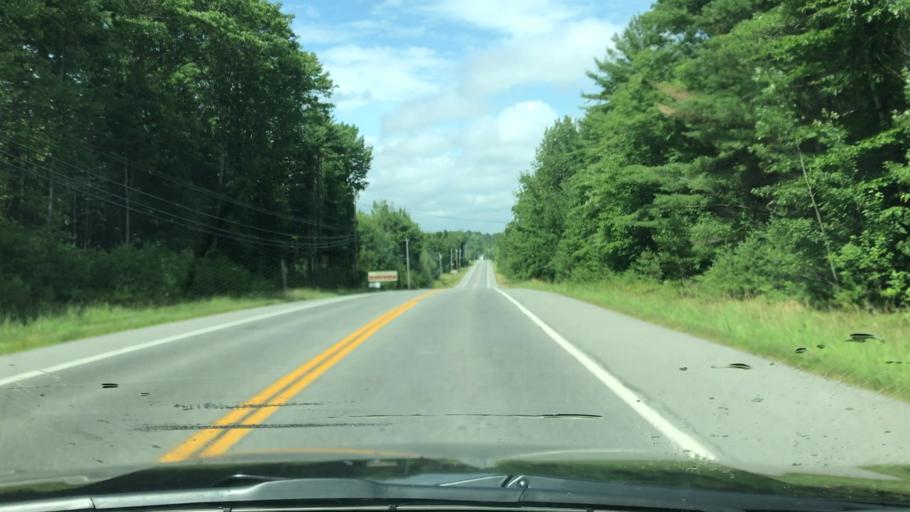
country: US
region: Maine
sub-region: Waldo County
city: Northport
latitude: 44.3737
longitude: -68.9841
